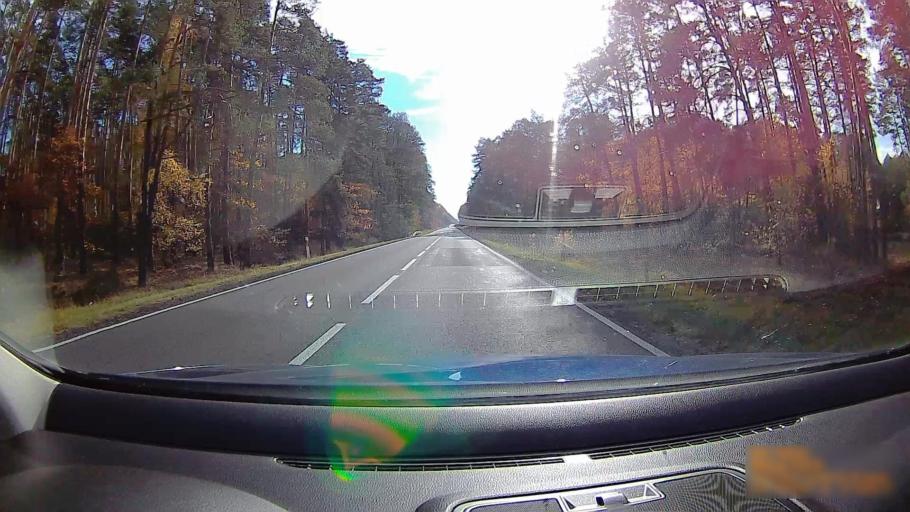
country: PL
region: Greater Poland Voivodeship
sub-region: Powiat ostrzeszowski
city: Ostrzeszow
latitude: 51.4619
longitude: 17.8995
